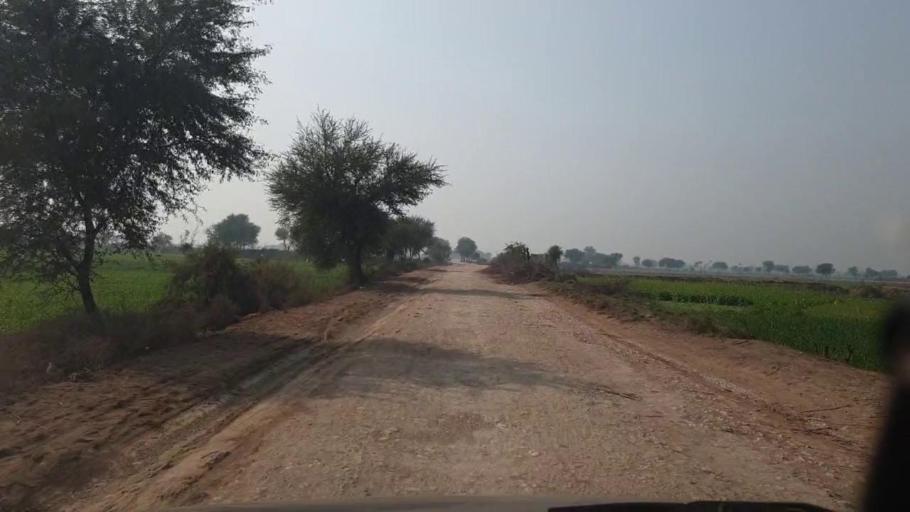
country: PK
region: Sindh
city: Shahdadpur
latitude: 26.0224
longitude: 68.5391
